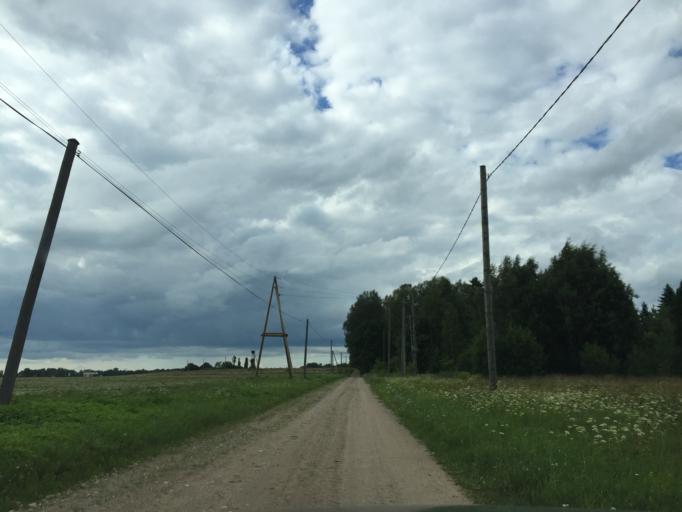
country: LV
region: Malpils
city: Malpils
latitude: 56.9940
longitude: 24.9679
